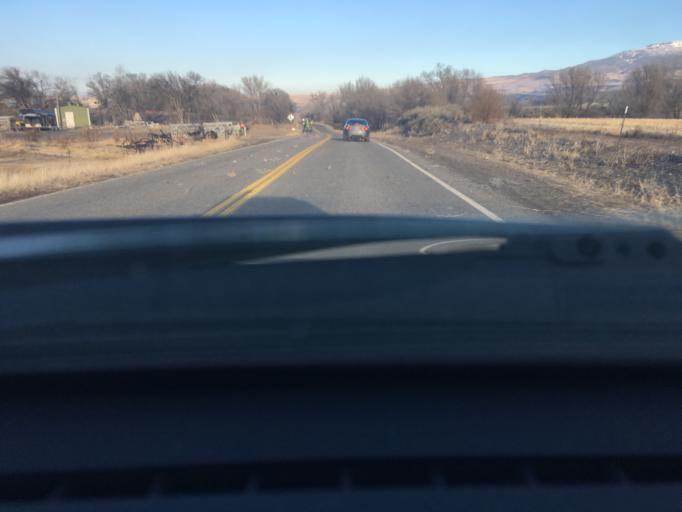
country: US
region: Colorado
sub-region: Delta County
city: Delta
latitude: 38.7416
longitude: -108.1105
